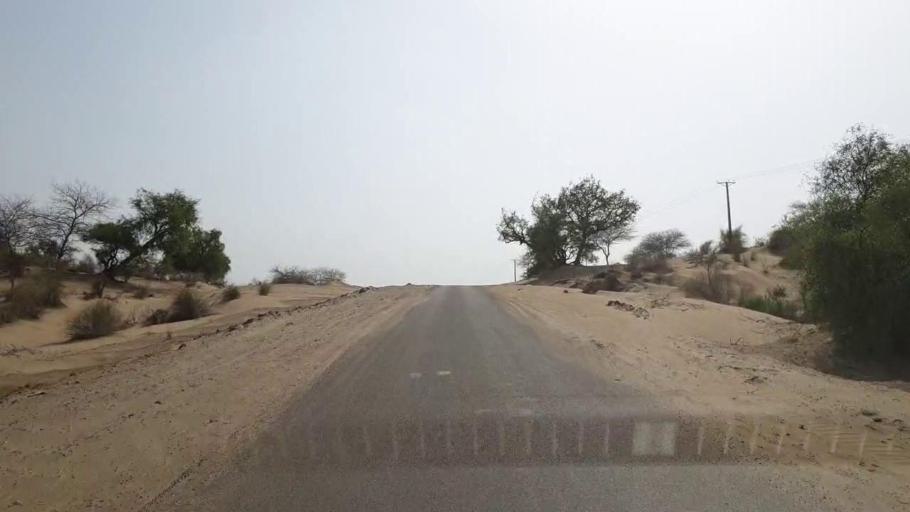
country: PK
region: Sindh
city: Mithi
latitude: 24.6208
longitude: 69.8978
